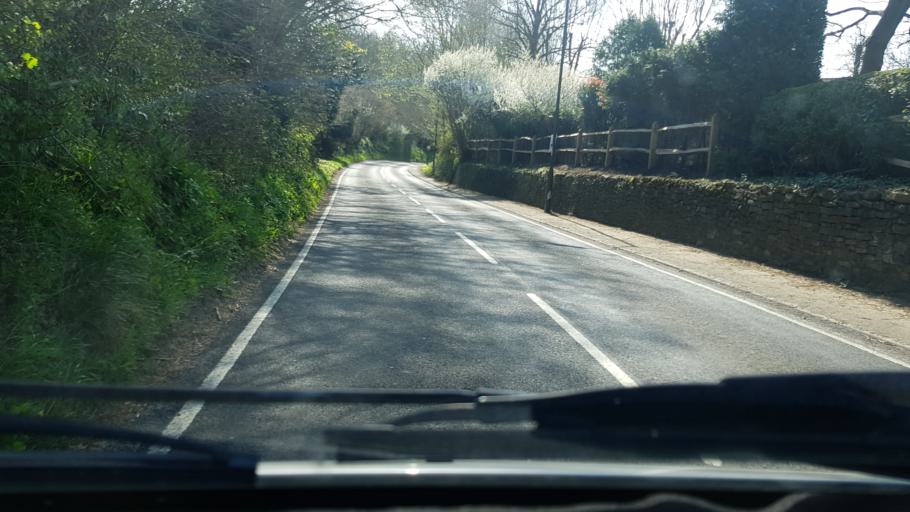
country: GB
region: England
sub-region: West Sussex
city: Midhurst
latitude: 51.0009
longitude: -0.7314
